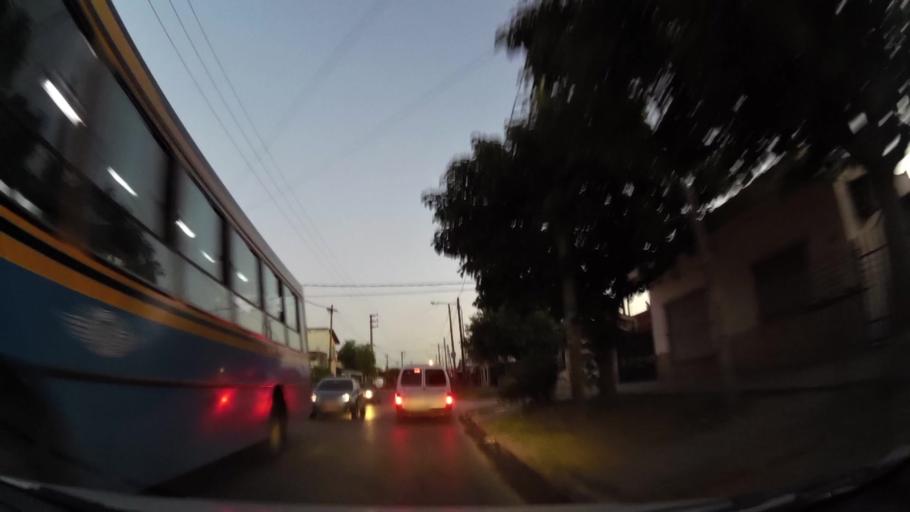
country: AR
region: Buenos Aires
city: San Justo
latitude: -34.7038
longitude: -58.6053
